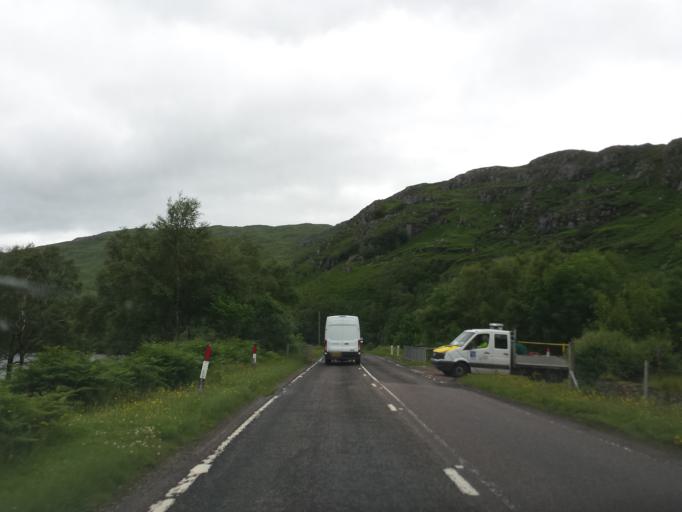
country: GB
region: Scotland
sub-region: Highland
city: Fort William
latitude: 56.8790
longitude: -5.5786
